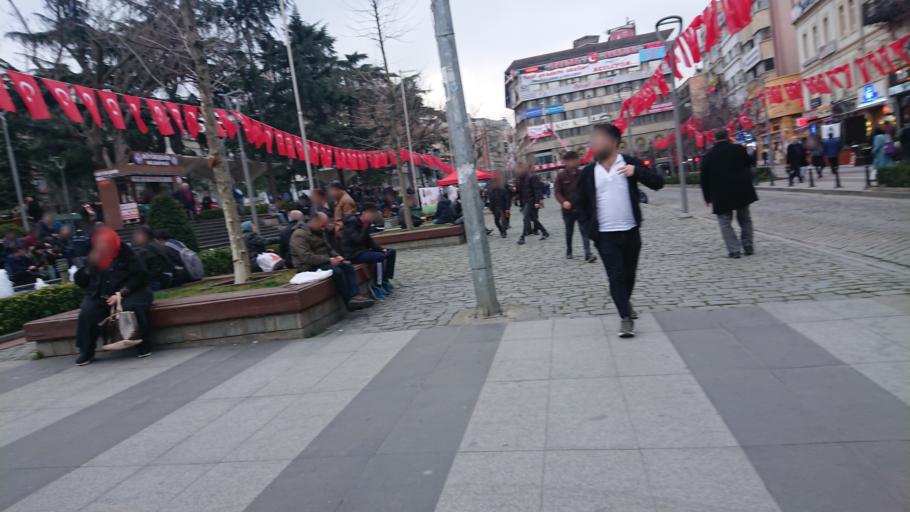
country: TR
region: Trabzon
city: Trabzon
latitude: 41.0056
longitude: 39.7314
